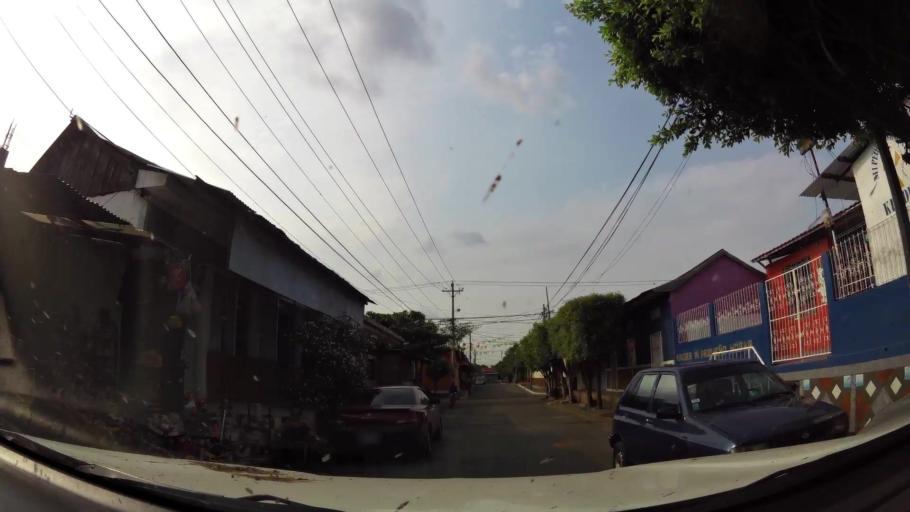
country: NI
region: Masaya
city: Masaya
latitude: 11.9774
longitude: -86.0918
